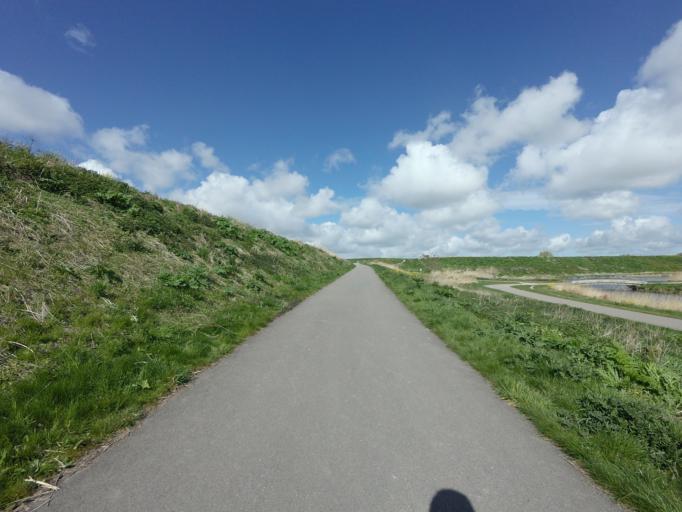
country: NL
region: South Holland
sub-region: Gemeente Lansingerland
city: Bleiswijk
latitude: 51.9757
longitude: 4.5426
